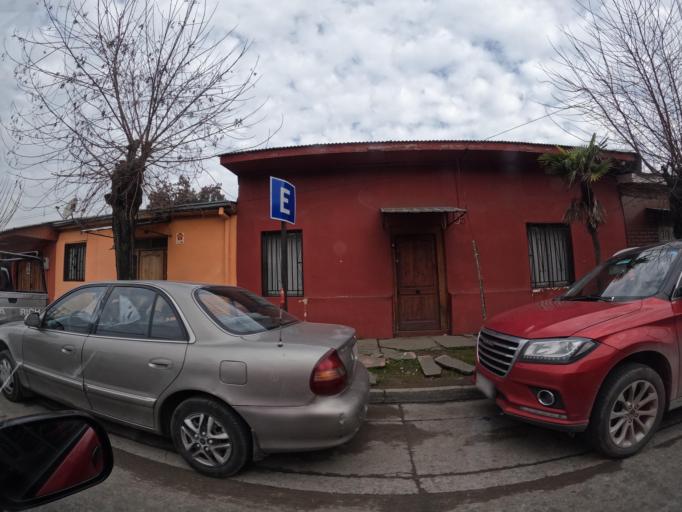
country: CL
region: Maule
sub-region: Provincia de Linares
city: Linares
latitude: -35.8576
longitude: -71.5806
